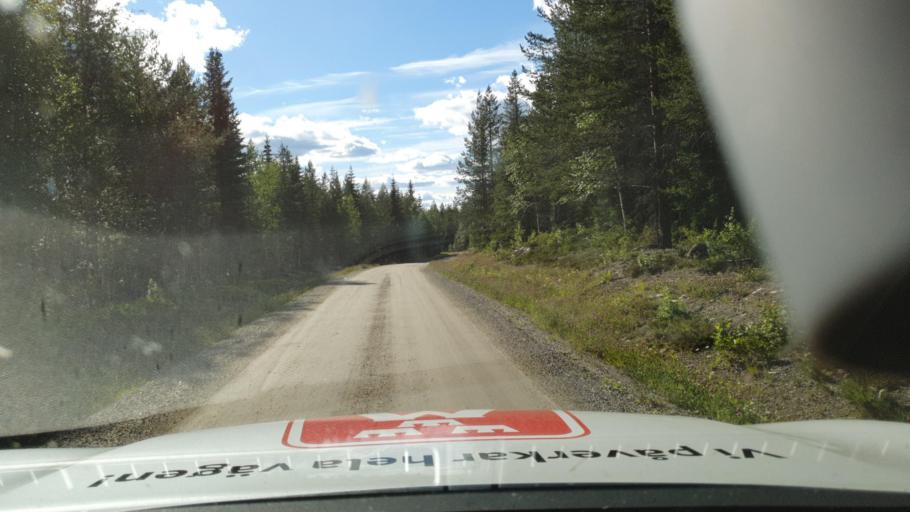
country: SE
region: Vaesterbotten
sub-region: Lycksele Kommun
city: Lycksele
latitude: 64.4101
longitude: 18.4994
